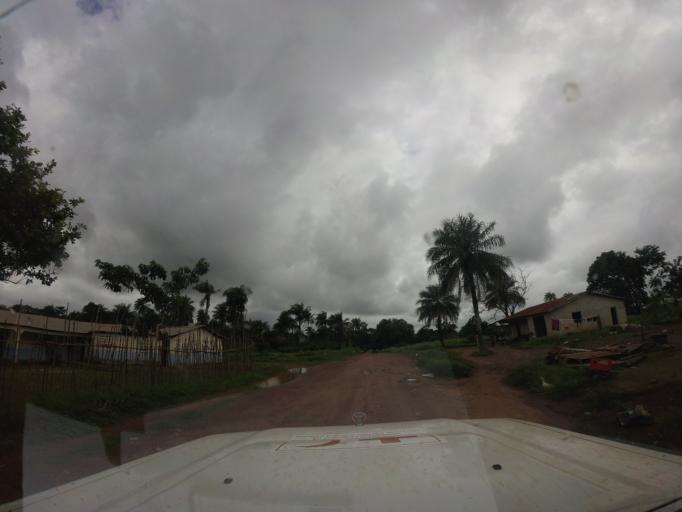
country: SL
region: Northern Province
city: Kukuna
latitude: 9.2801
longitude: -12.6729
